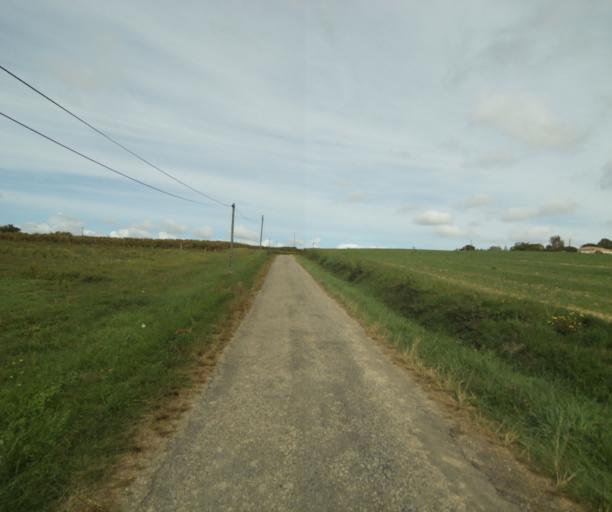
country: FR
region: Midi-Pyrenees
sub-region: Departement du Gers
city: Eauze
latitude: 43.8416
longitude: 0.1415
